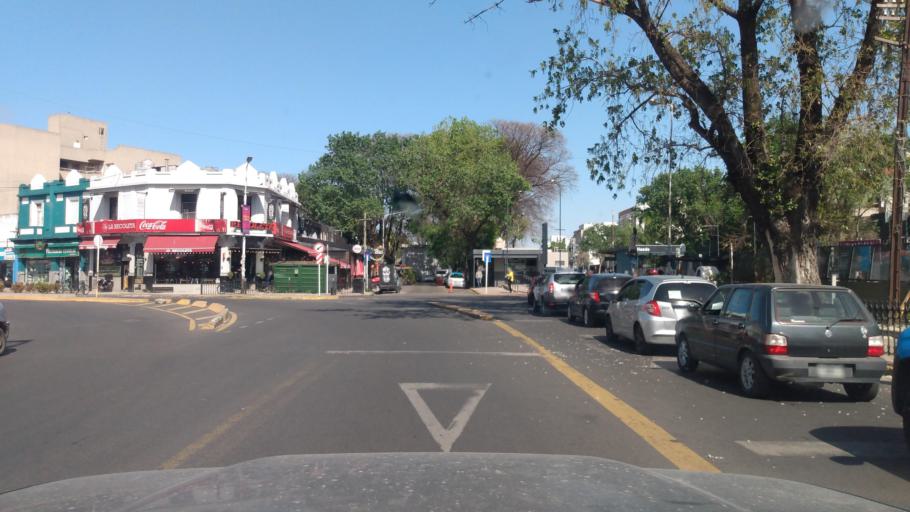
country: AR
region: Buenos Aires
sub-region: Partido de Moron
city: Moron
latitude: -34.6445
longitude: -58.5899
